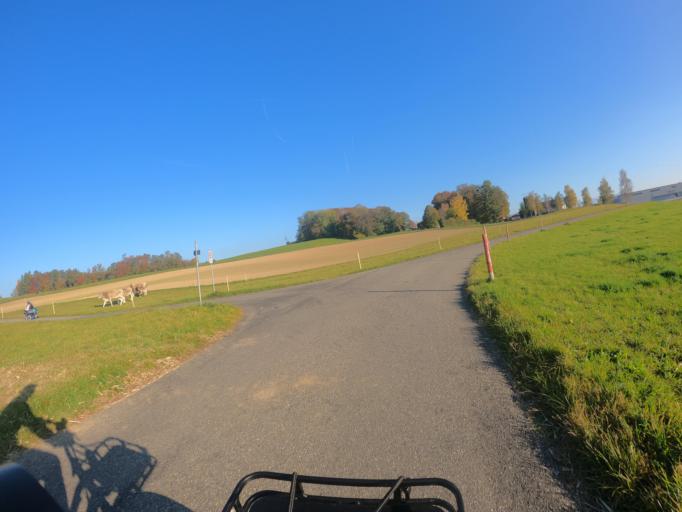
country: CH
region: Zurich
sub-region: Bezirk Affoltern
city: Affoltern / Oberdorf
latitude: 47.2799
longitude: 8.4357
